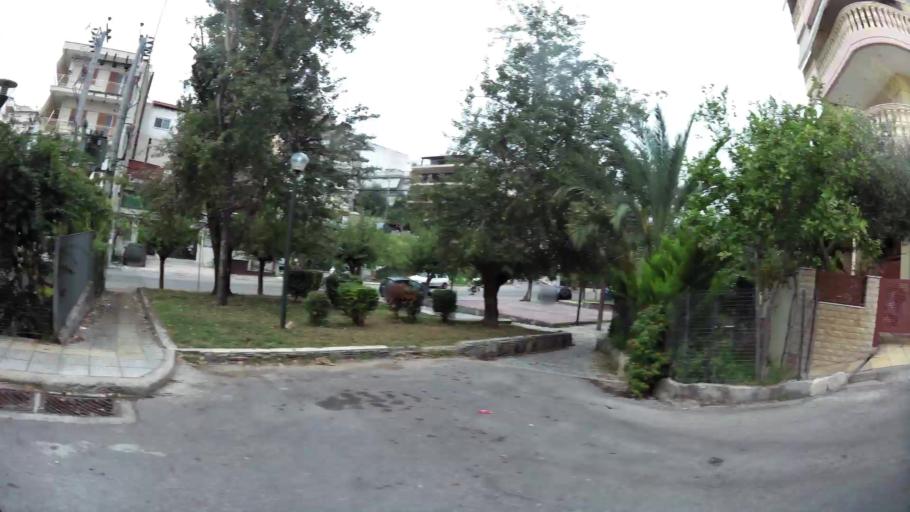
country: GR
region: Attica
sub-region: Nomarchia Athinas
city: Chaidari
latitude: 38.0058
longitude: 23.6683
